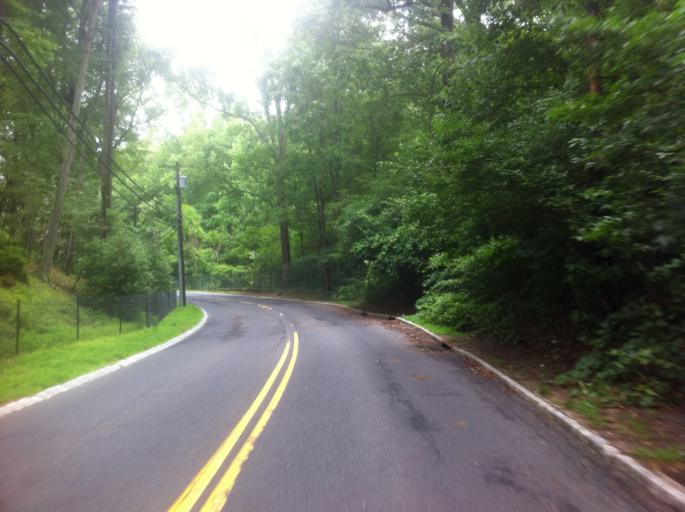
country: US
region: New York
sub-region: Nassau County
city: Bayville
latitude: 40.8870
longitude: -73.5549
